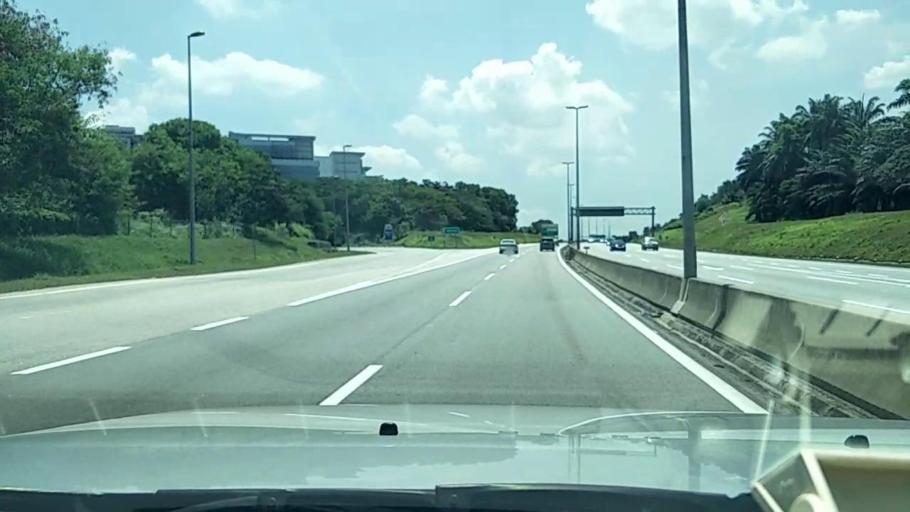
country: MY
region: Putrajaya
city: Putrajaya
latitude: 2.9339
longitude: 101.6579
